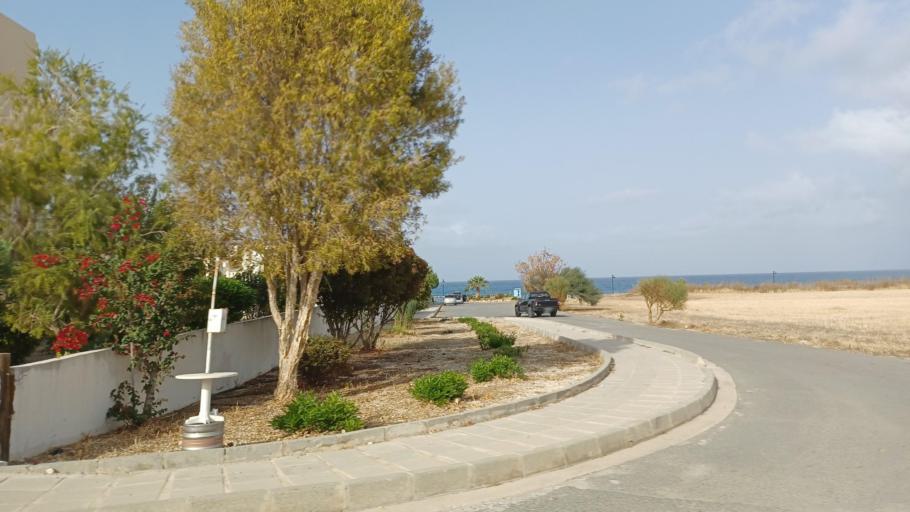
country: CY
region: Pafos
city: Polis
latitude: 35.0391
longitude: 32.4097
